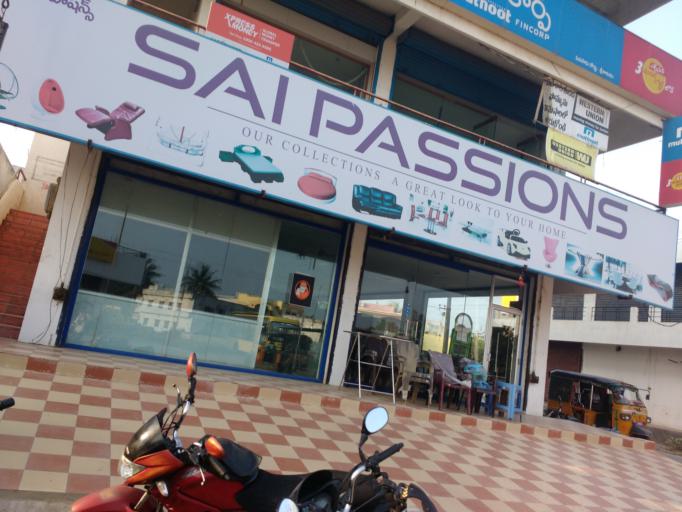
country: IN
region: Andhra Pradesh
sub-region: Srikakulam
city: Srikakulam
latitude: 18.3023
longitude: 83.9088
